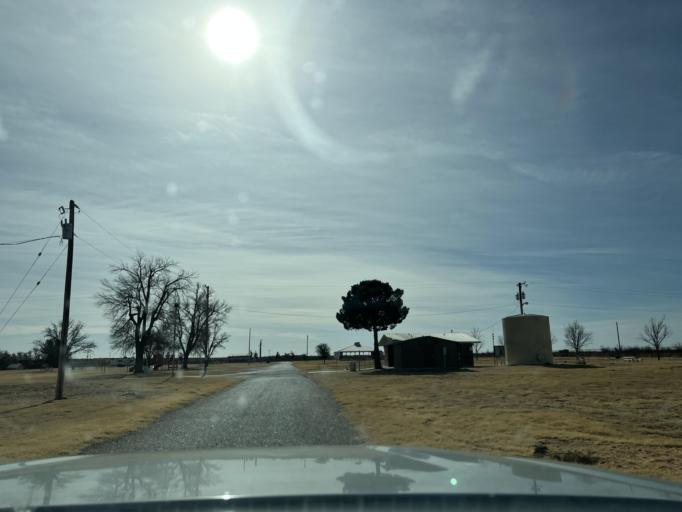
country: US
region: Texas
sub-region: Andrews County
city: Andrews
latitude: 32.4549
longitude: -102.5706
